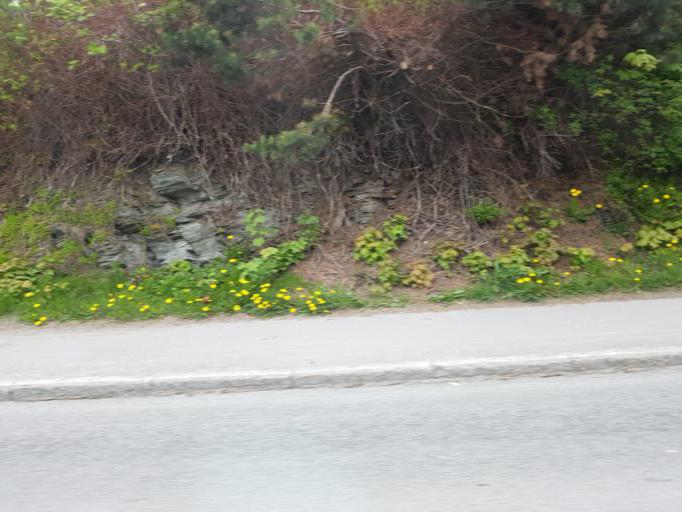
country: NO
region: Nord-Trondelag
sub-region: Levanger
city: Levanger
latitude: 63.7476
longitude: 11.2879
